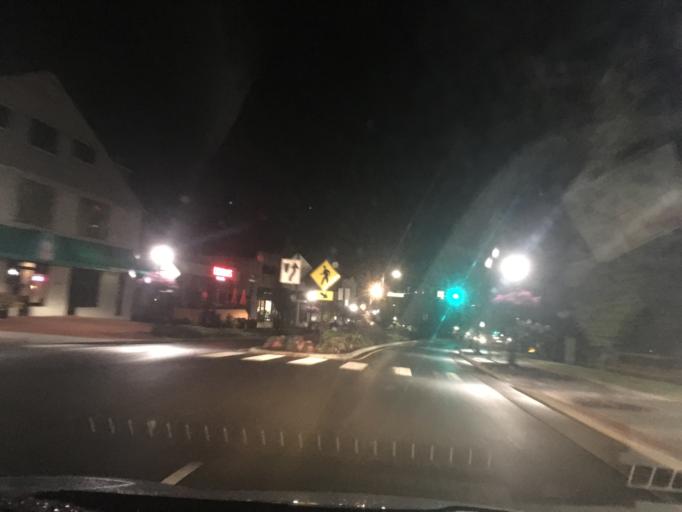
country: US
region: Virginia
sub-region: Montgomery County
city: Blacksburg
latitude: 37.2321
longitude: -80.4167
